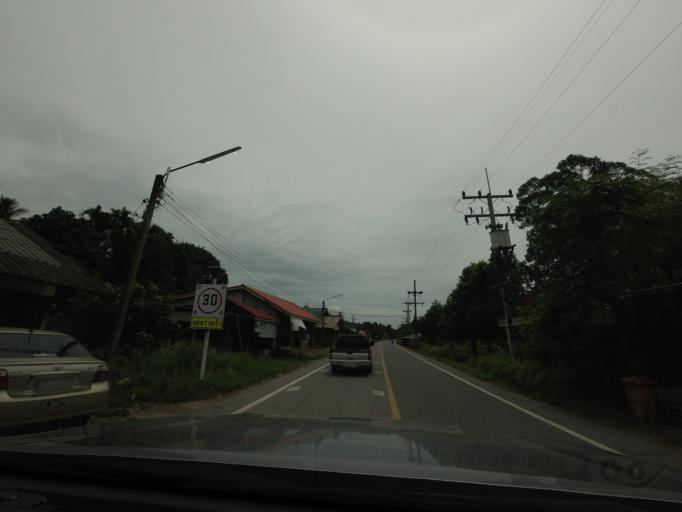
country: TH
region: Pattani
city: Kapho
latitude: 6.6356
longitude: 101.5492
